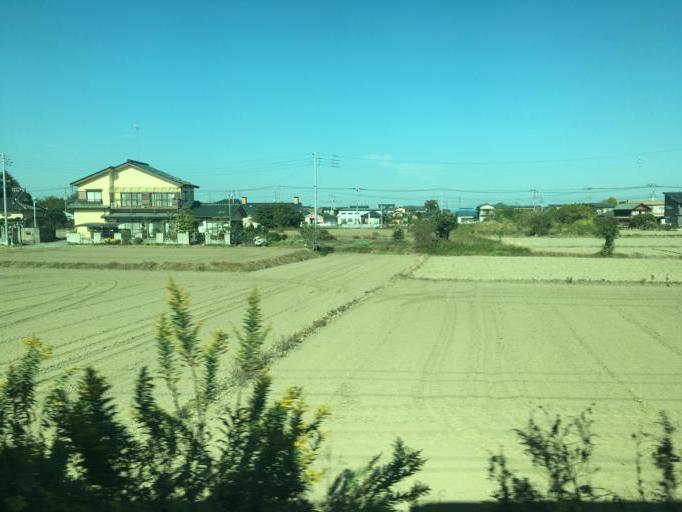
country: JP
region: Ibaraki
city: Yuki
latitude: 36.2969
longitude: 139.8895
